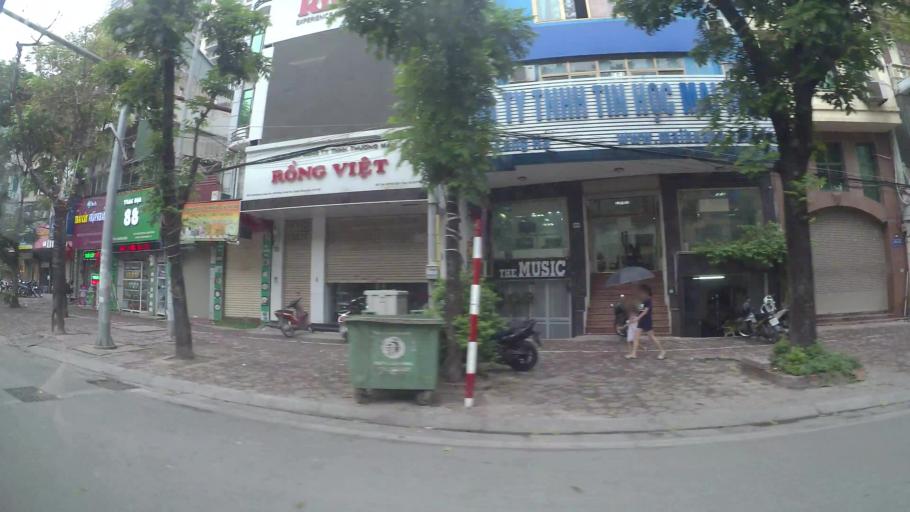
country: VN
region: Ha Noi
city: Dong Da
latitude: 21.0128
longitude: 105.8123
